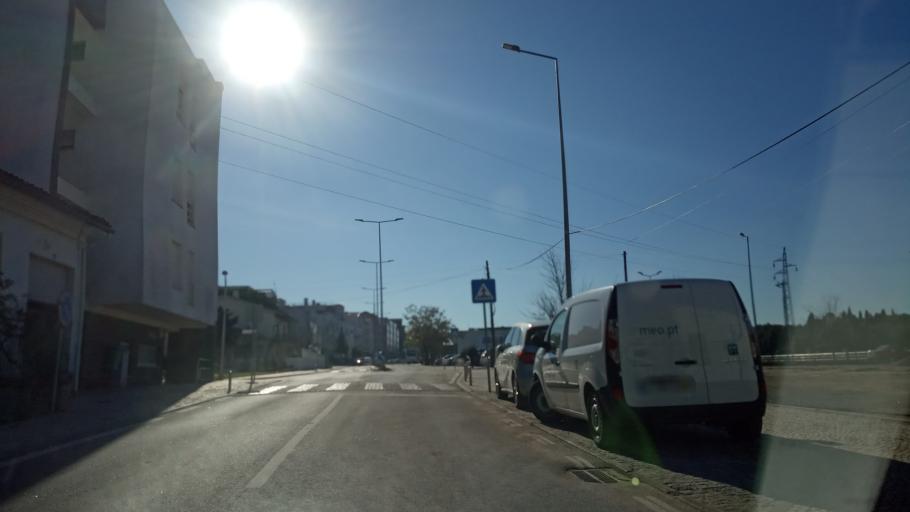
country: PT
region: Aveiro
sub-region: Anadia
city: Anadia
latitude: 40.4394
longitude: -8.4365
